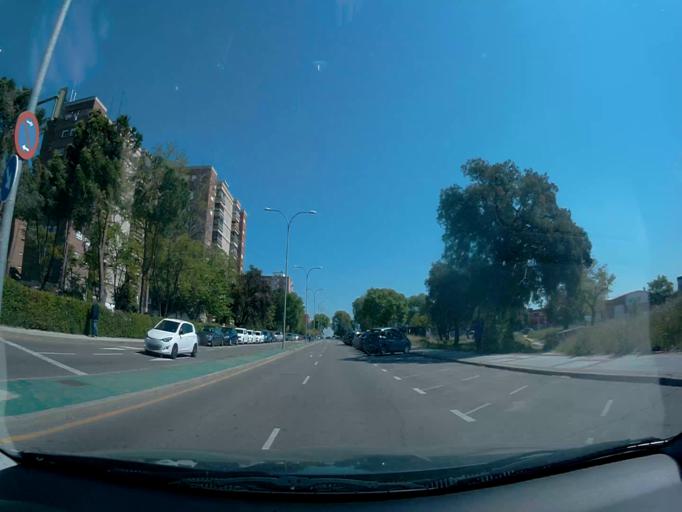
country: ES
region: Madrid
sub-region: Provincia de Madrid
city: Alcorcon
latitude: 40.3482
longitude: -3.8040
